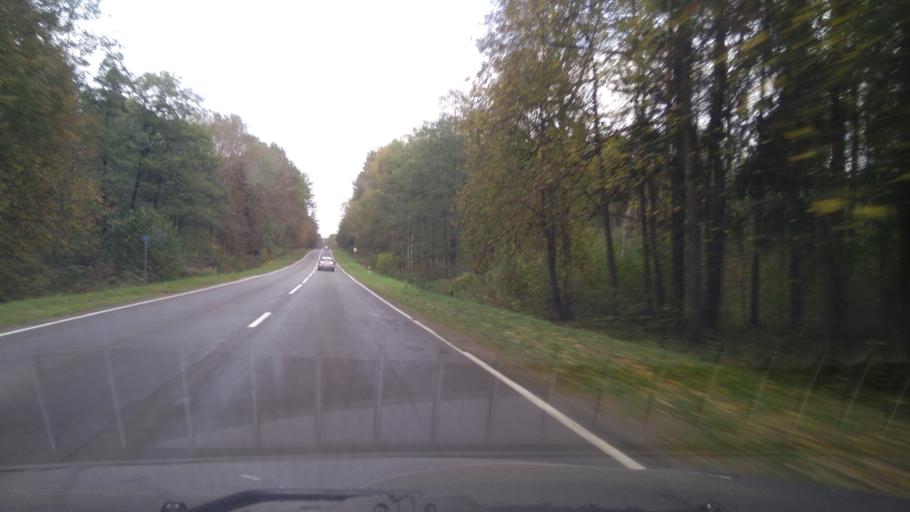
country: BY
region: Minsk
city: Druzhny
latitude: 53.6309
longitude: 27.8837
